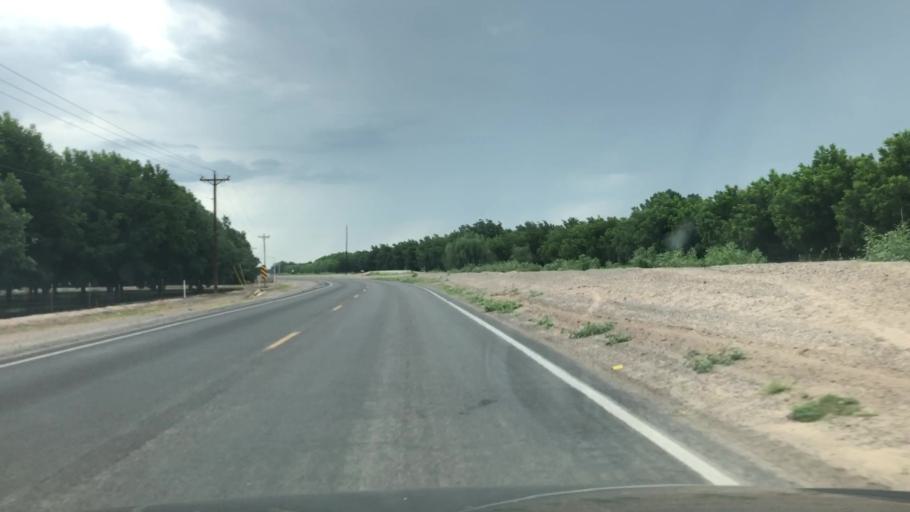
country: US
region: New Mexico
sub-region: Dona Ana County
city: La Union
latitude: 31.9909
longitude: -106.6512
